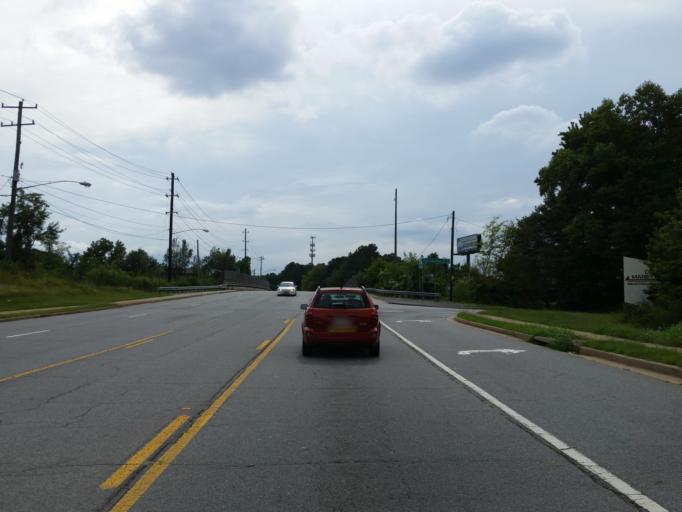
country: US
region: Georgia
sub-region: Cobb County
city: Marietta
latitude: 33.9733
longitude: -84.5293
